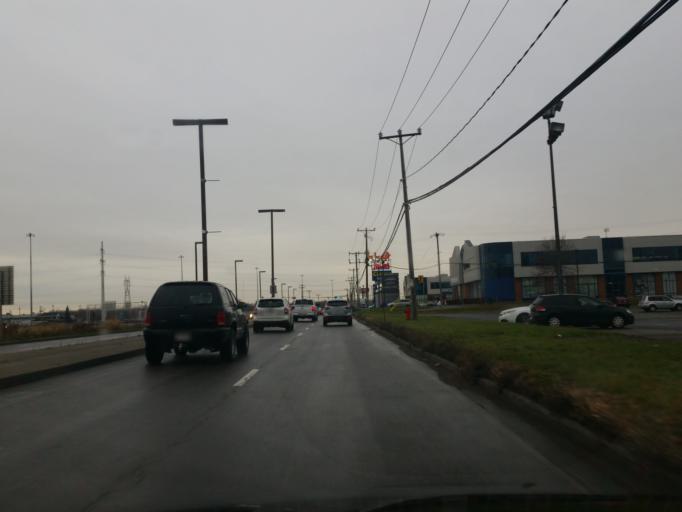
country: CA
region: Quebec
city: Quebec
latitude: 46.8300
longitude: -71.2843
